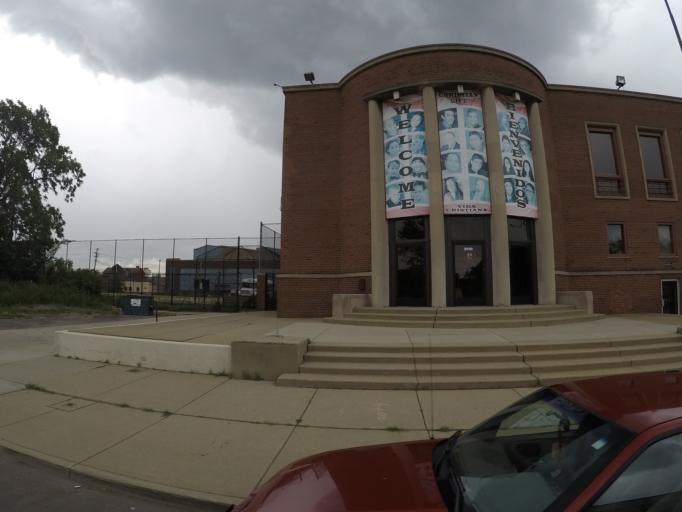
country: US
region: Michigan
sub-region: Wayne County
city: Dearborn
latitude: 42.3297
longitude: -83.1192
